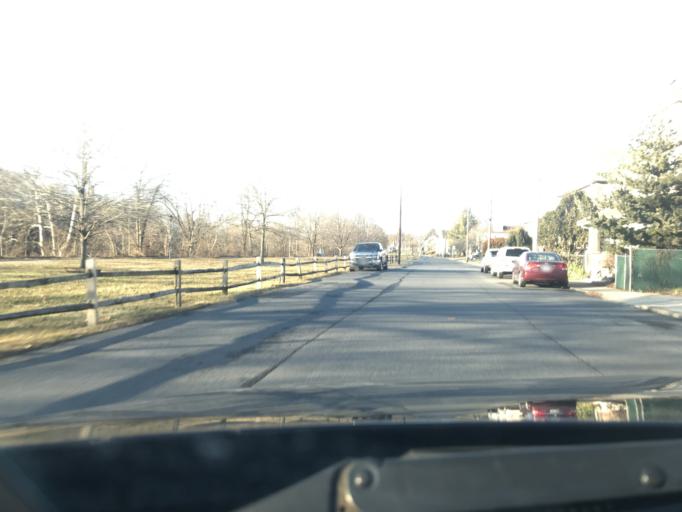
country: US
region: Pennsylvania
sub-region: Northampton County
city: Northampton
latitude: 40.6824
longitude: -75.4985
